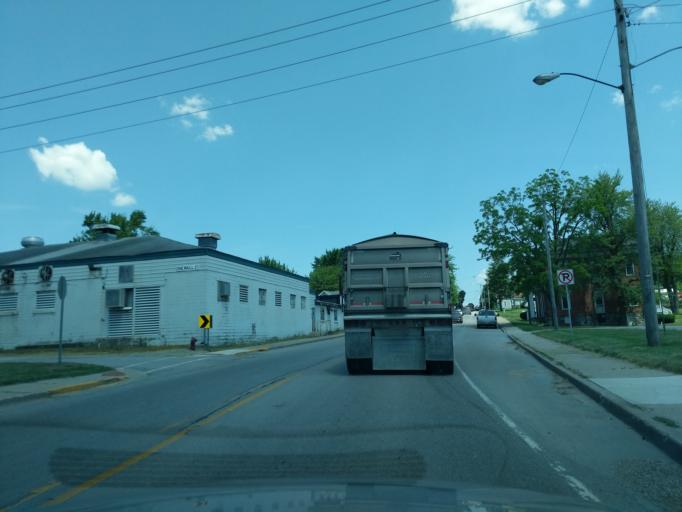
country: US
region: Indiana
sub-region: Noble County
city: Ligonier
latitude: 41.4688
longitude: -85.5878
